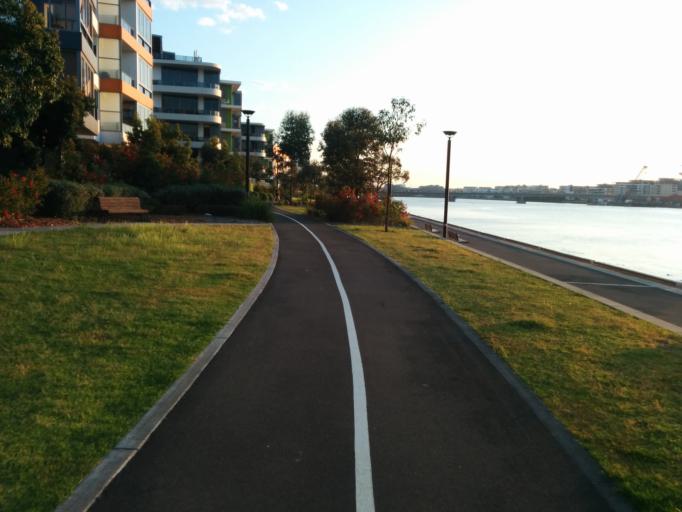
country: AU
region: New South Wales
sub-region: Canada Bay
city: Rhodes
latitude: -33.8239
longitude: 151.0866
